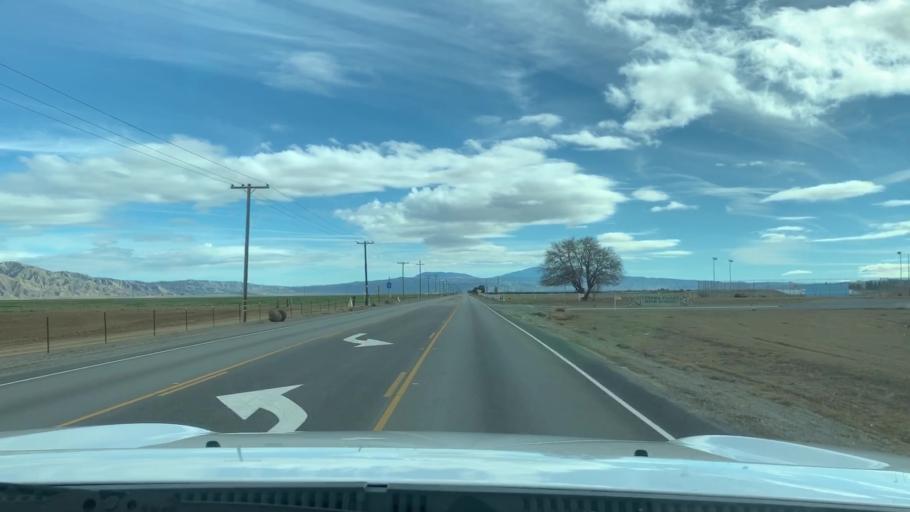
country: US
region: California
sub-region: Kern County
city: Taft Heights
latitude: 34.9452
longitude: -119.6760
